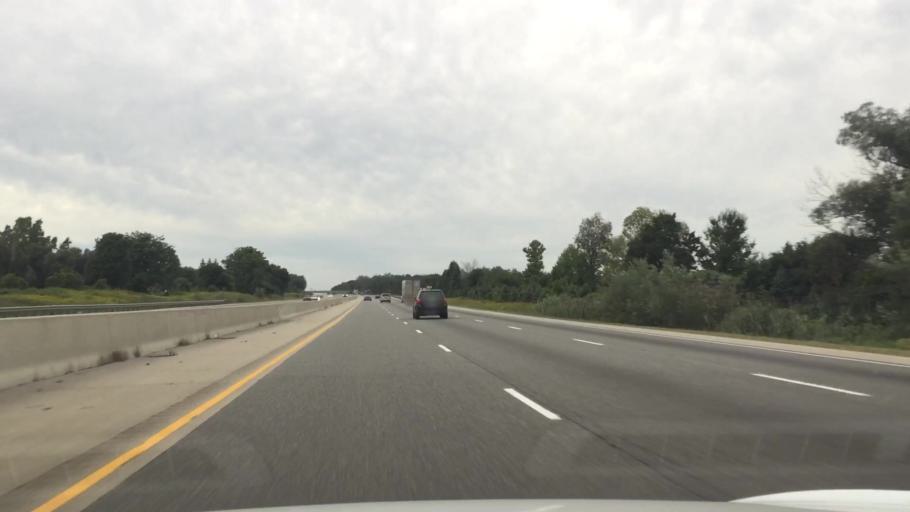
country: CA
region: Ontario
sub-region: Oxford County
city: Woodstock
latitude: 43.1736
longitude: -80.6549
